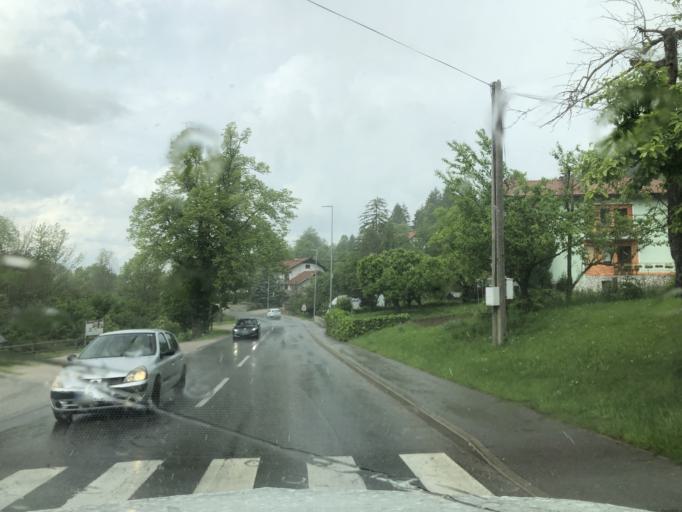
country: SI
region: Cerknica
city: Cerknica
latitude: 45.7772
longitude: 14.4002
